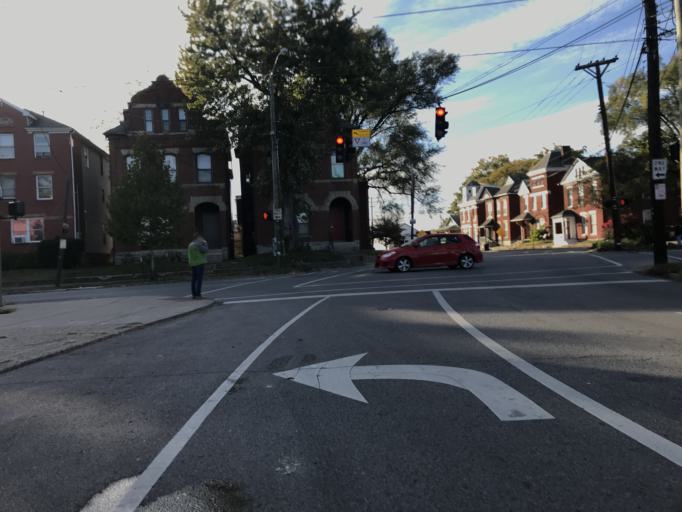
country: US
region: Kentucky
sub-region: Jefferson County
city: Louisville
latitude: 38.2422
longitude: -85.7621
